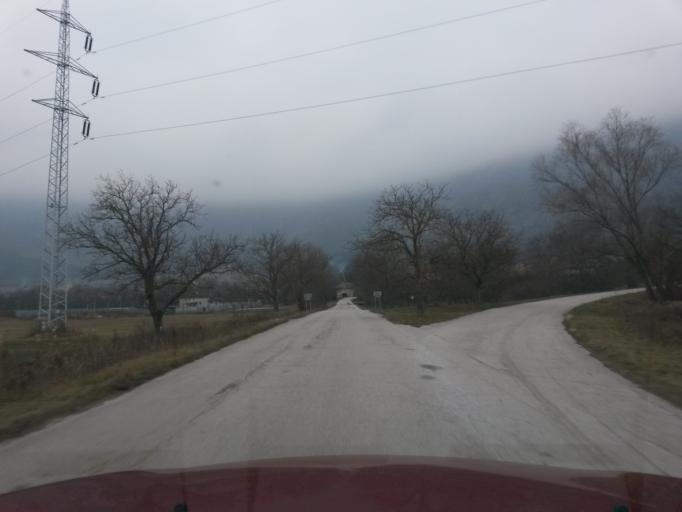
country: SK
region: Kosicky
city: Medzev
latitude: 48.6029
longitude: 20.7577
